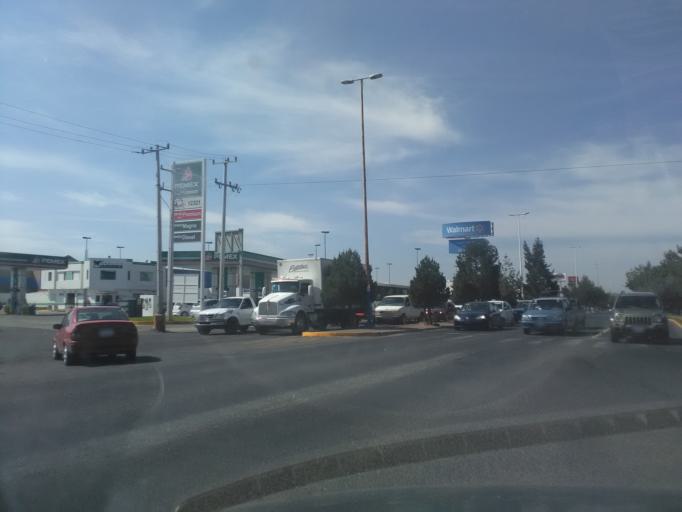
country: MX
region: Durango
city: Victoria de Durango
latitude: 24.0578
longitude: -104.6117
